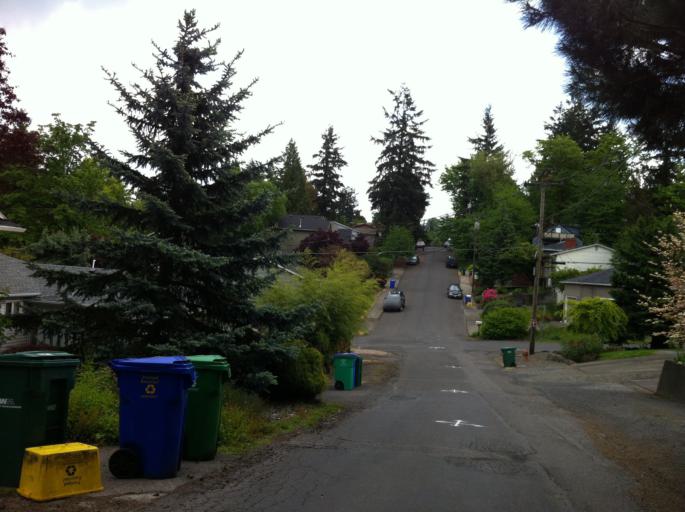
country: US
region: Oregon
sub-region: Clackamas County
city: Lake Oswego
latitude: 45.4655
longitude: -122.6937
